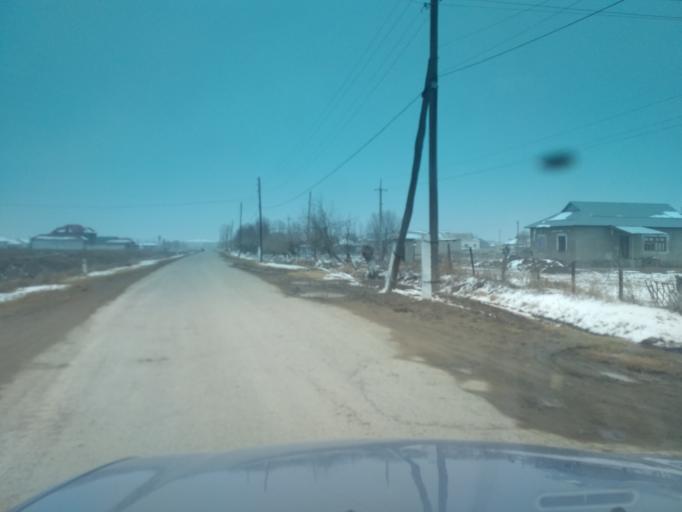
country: UZ
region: Sirdaryo
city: Guliston
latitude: 40.4786
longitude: 68.7509
